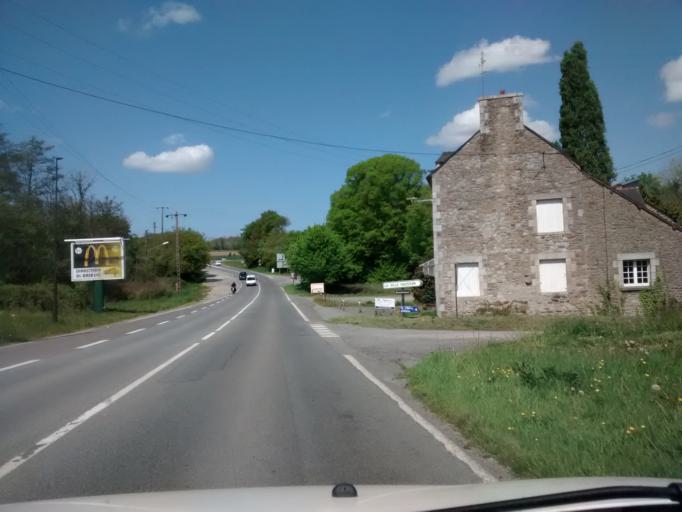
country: FR
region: Brittany
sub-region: Departement des Cotes-d'Armor
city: Saint-Samson-sur-Rance
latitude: 48.4781
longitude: -2.0420
